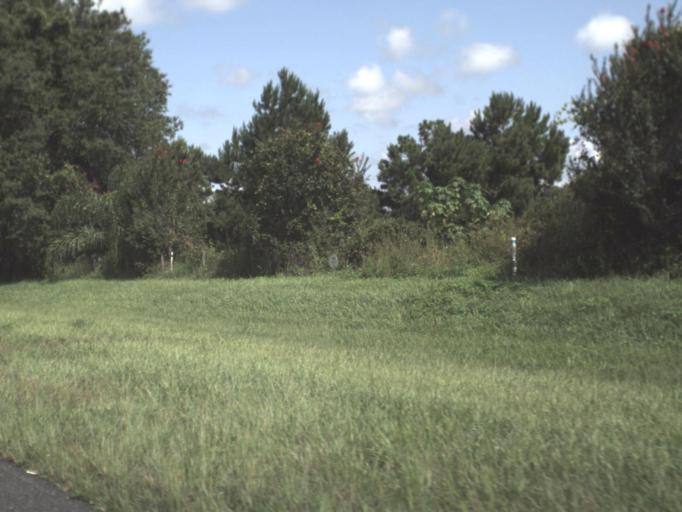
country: US
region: Florida
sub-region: Hernando County
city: Brooksville
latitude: 28.5374
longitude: -82.3437
